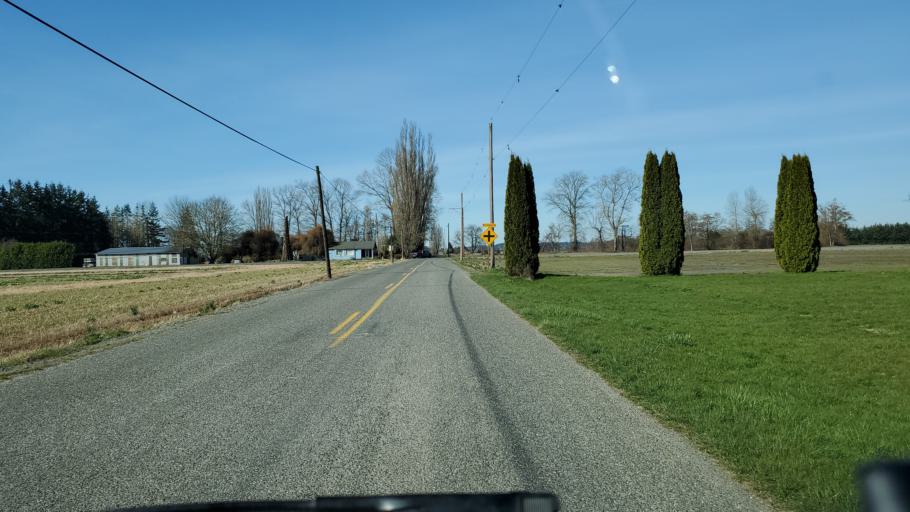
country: US
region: Washington
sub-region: Skagit County
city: Mount Vernon
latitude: 48.3702
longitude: -122.3766
